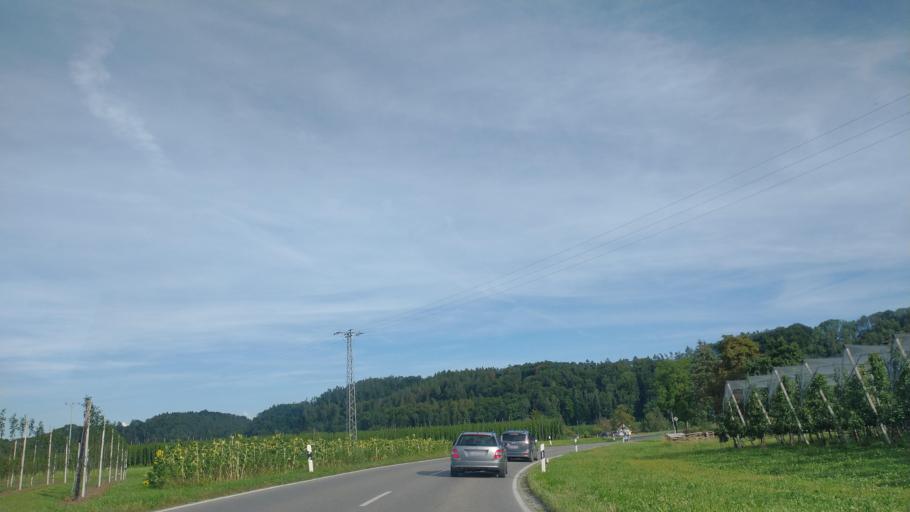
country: DE
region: Baden-Wuerttemberg
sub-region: Tuebingen Region
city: Kressbronn am Bodensee
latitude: 47.6287
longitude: 9.6006
